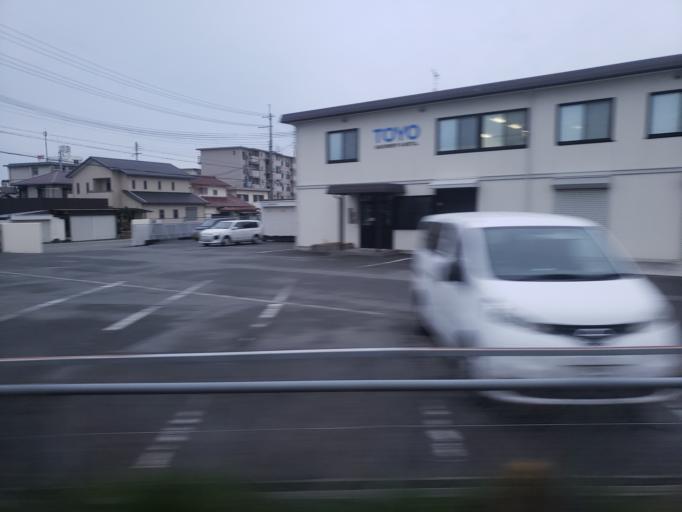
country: JP
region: Hyogo
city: Kakogawacho-honmachi
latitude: 34.7129
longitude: 134.8933
